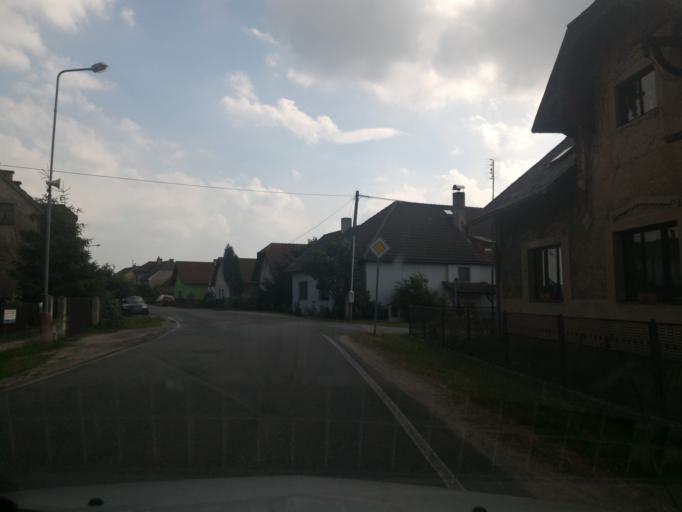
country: CZ
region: Central Bohemia
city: Loucen
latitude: 50.2760
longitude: 15.0134
